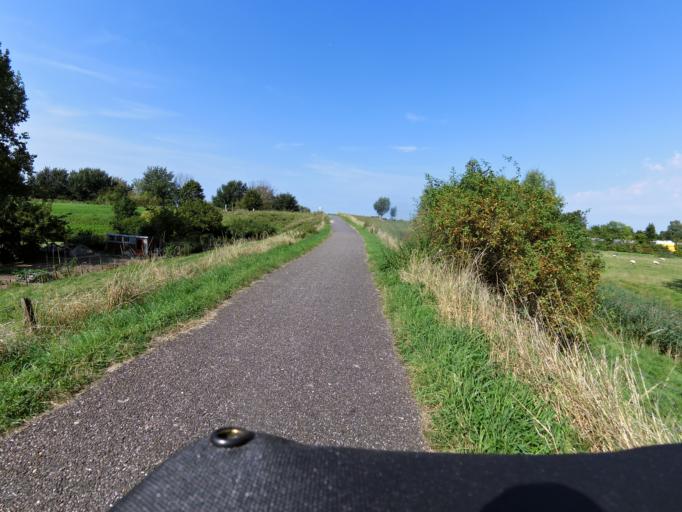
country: NL
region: South Holland
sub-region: Gemeente Oud-Beijerland
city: Oud-Beijerland
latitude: 51.8282
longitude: 4.4275
